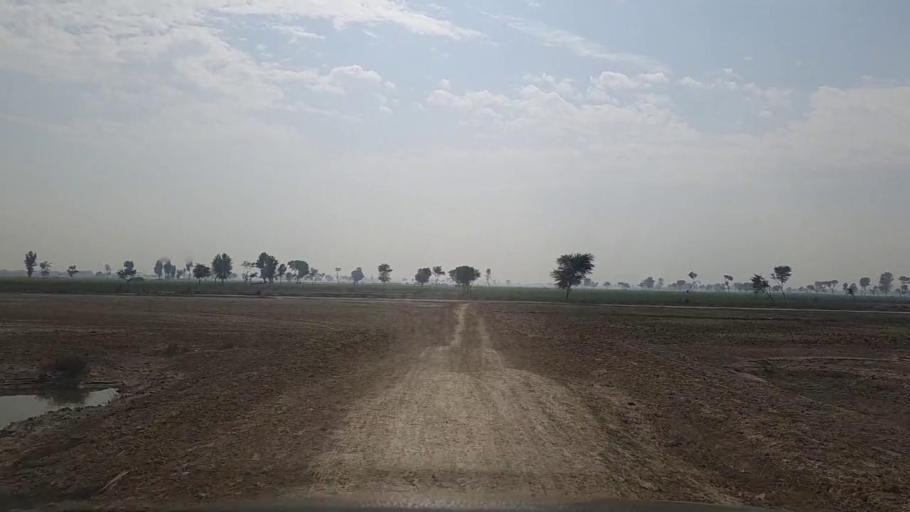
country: PK
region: Sindh
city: Daur
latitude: 26.3803
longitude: 68.3823
